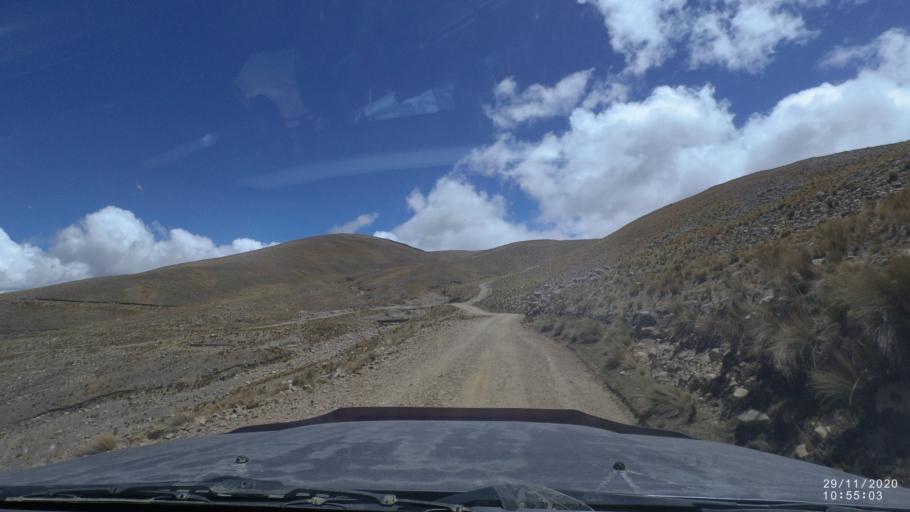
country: BO
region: Cochabamba
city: Cochabamba
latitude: -17.2244
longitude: -66.2218
